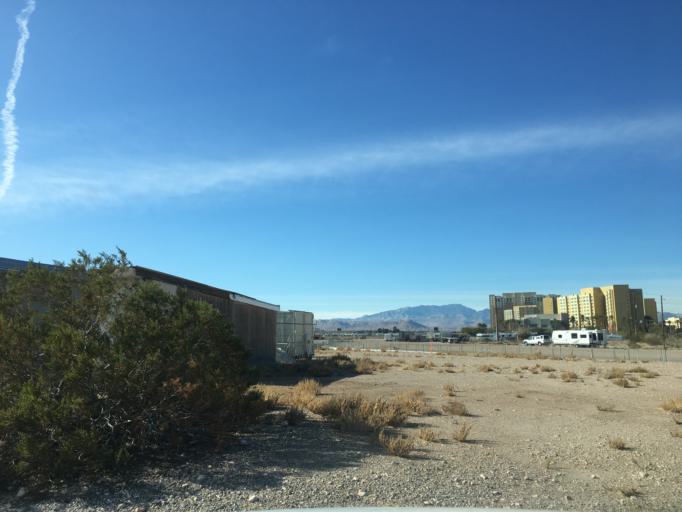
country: US
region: Nevada
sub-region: Clark County
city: Enterprise
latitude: 36.0090
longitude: -115.1680
